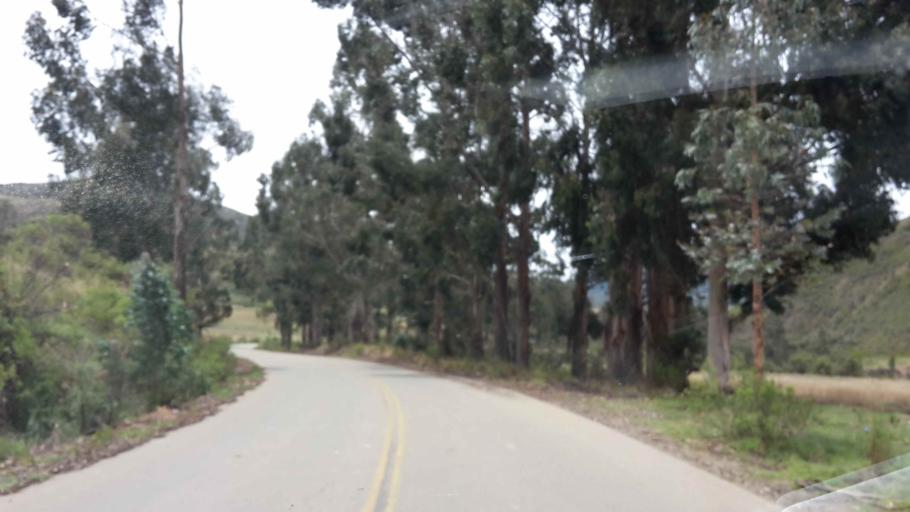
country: BO
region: Cochabamba
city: Totora
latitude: -17.6675
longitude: -65.2224
